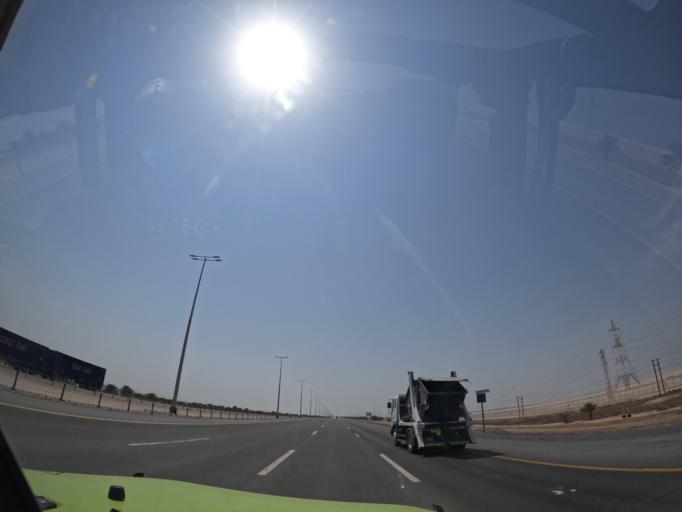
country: AE
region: Abu Dhabi
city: Abu Dhabi
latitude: 24.2045
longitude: 54.4020
